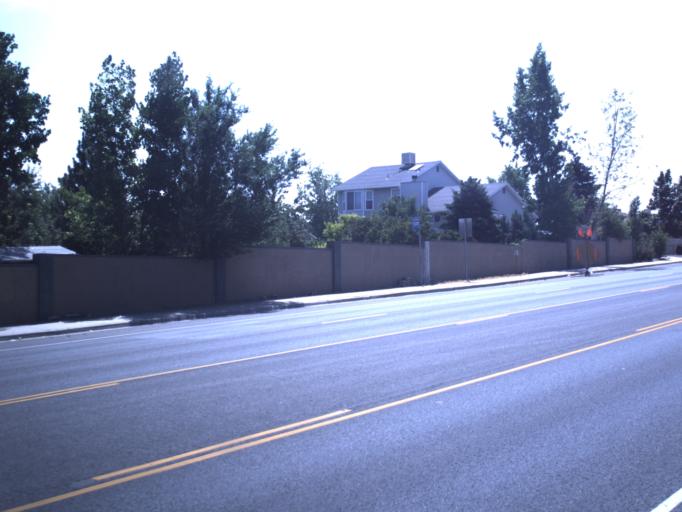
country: US
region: Utah
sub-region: Salt Lake County
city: West Valley City
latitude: 40.6753
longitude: -112.0248
